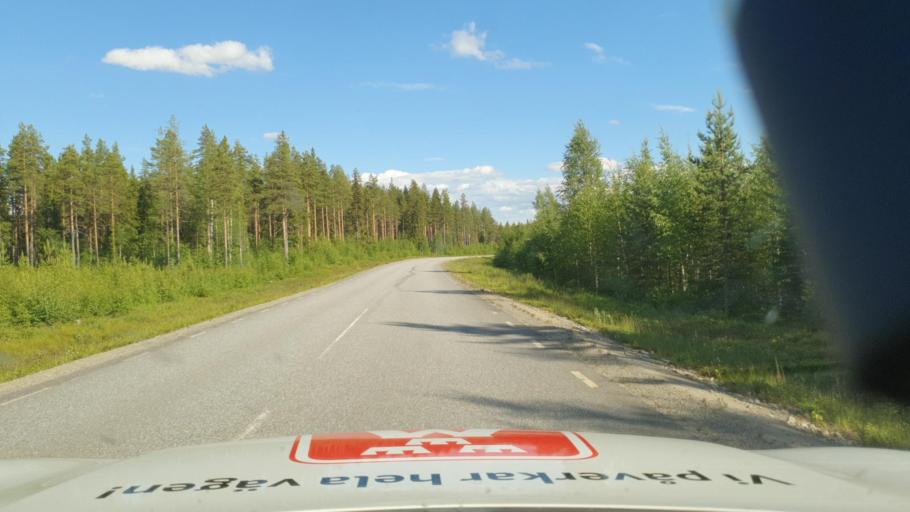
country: SE
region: Vaesterbotten
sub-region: Skelleftea Kommun
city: Langsele
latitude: 64.8407
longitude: 19.8785
